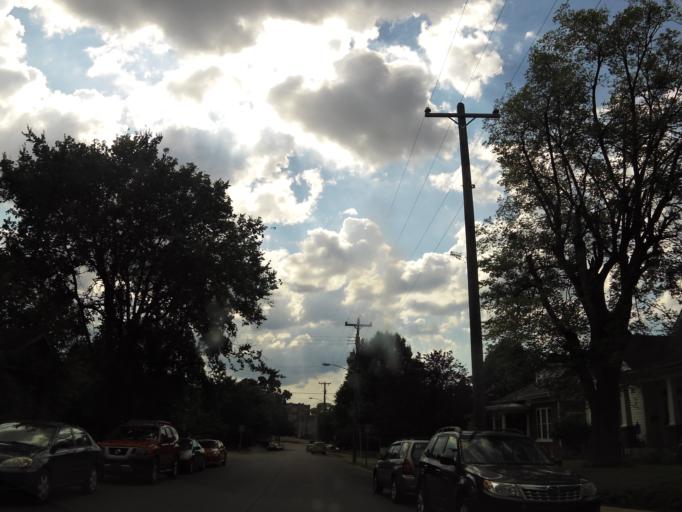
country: US
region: Tennessee
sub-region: Davidson County
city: Nashville
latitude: 36.1804
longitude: -86.7474
